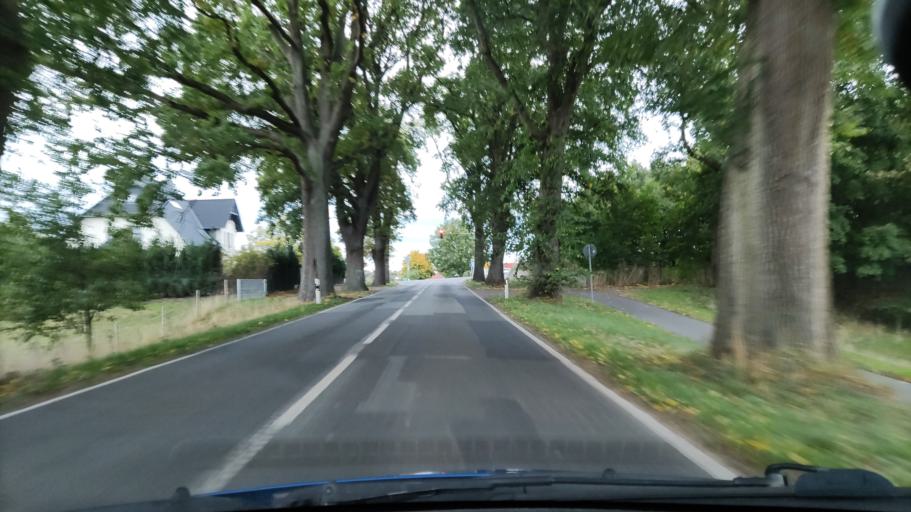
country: DE
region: Mecklenburg-Vorpommern
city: Lubtheen
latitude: 53.3930
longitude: 10.9651
